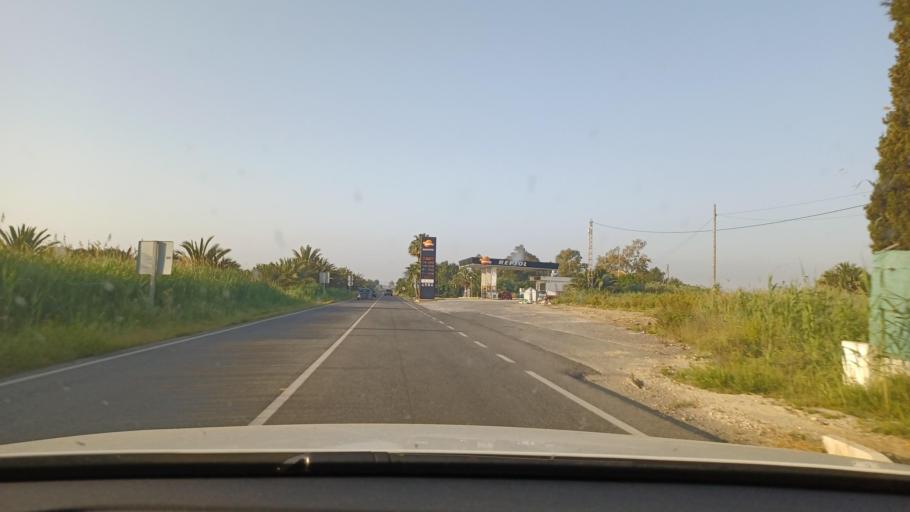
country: ES
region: Valencia
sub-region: Provincia de Alicante
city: Dolores
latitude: 38.1782
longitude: -0.7018
